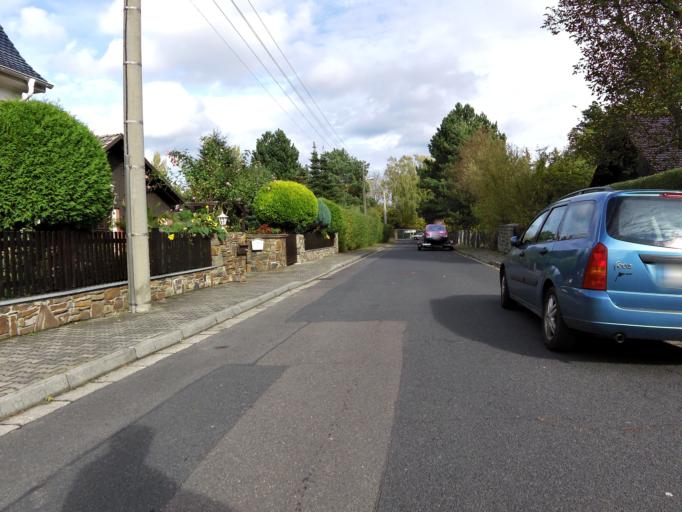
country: DE
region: Saxony
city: Grossposna
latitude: 51.2973
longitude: 12.4531
